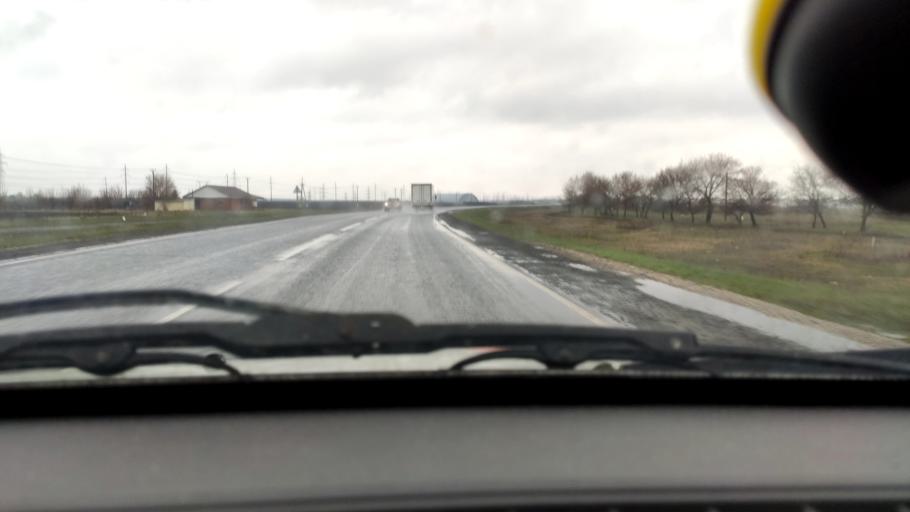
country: RU
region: Samara
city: Povolzhskiy
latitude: 53.6409
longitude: 49.6617
